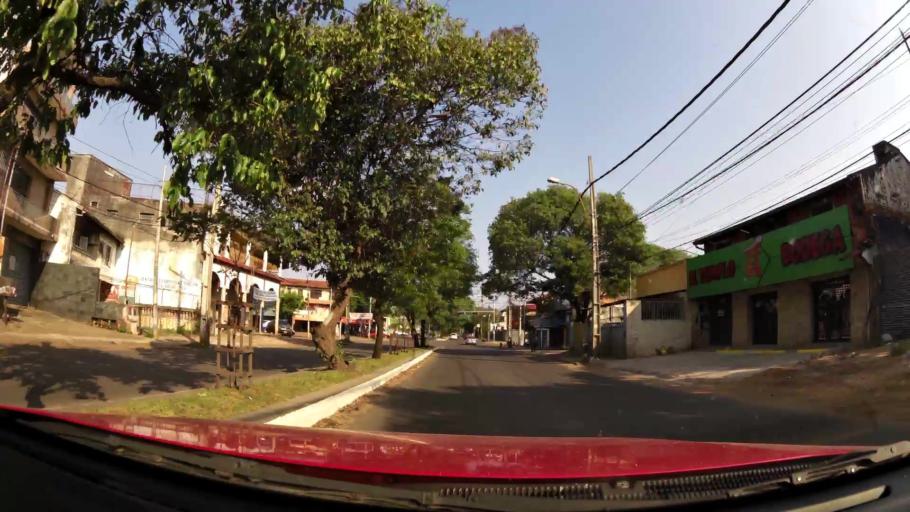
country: PY
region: Asuncion
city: Asuncion
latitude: -25.3128
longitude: -57.6118
